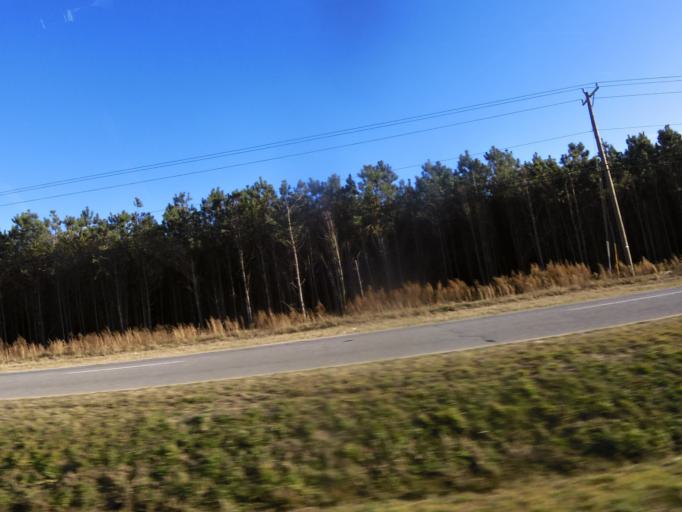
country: US
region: Virginia
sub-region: City of Suffolk
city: South Suffolk
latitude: 36.7112
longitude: -76.6768
